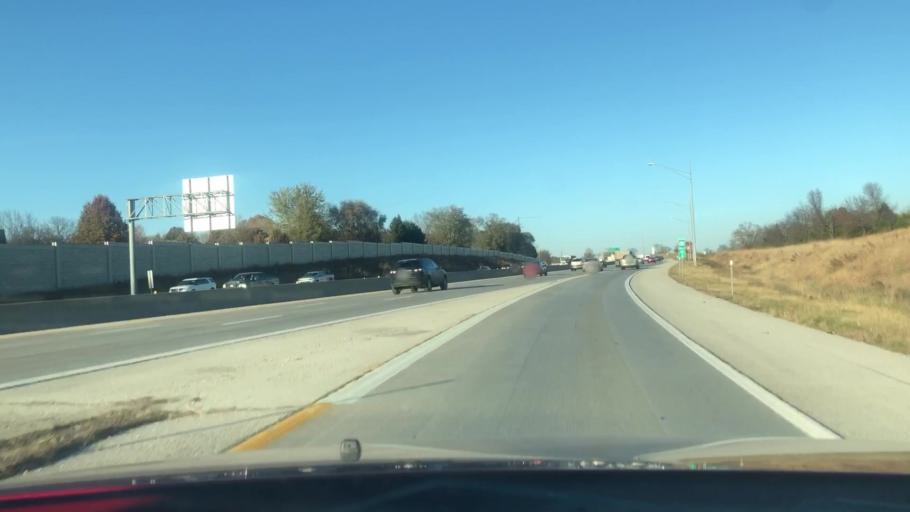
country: US
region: Missouri
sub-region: Greene County
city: Springfield
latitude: 37.1329
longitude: -93.2271
